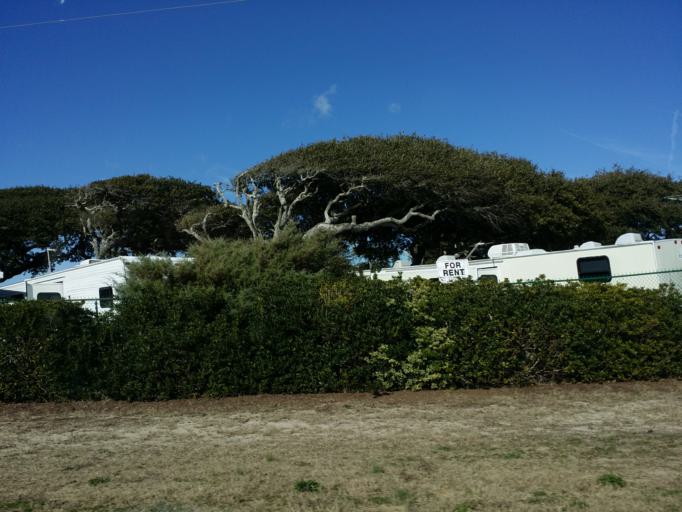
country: US
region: North Carolina
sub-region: Onslow County
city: Sneads Ferry
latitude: 34.4790
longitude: -77.4496
